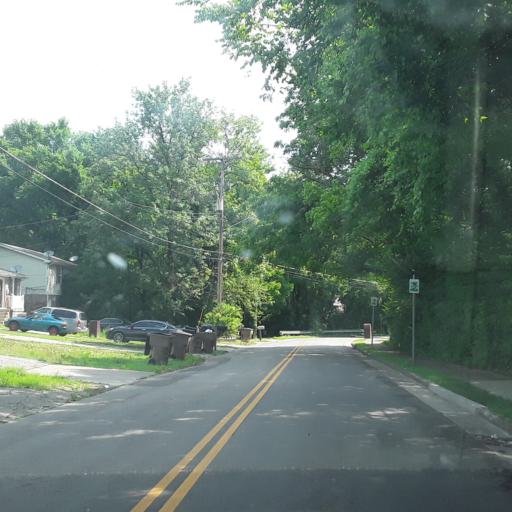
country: US
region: Tennessee
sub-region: Davidson County
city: Oak Hill
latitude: 36.1154
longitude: -86.7347
